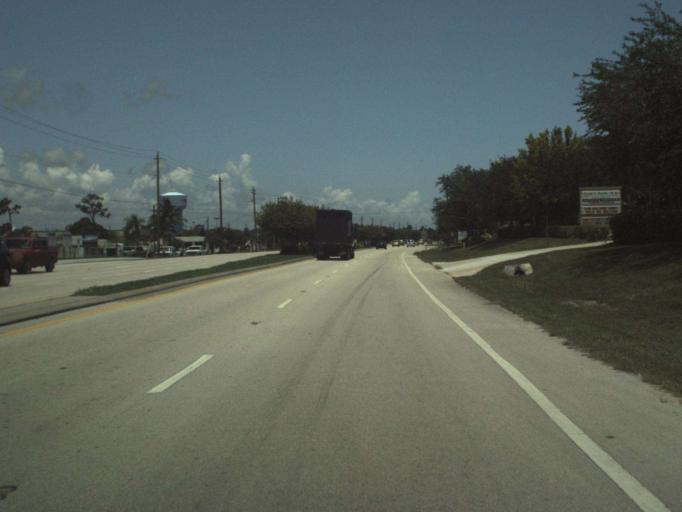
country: US
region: Florida
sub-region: Indian River County
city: Roseland
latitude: 27.8335
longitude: -80.4822
